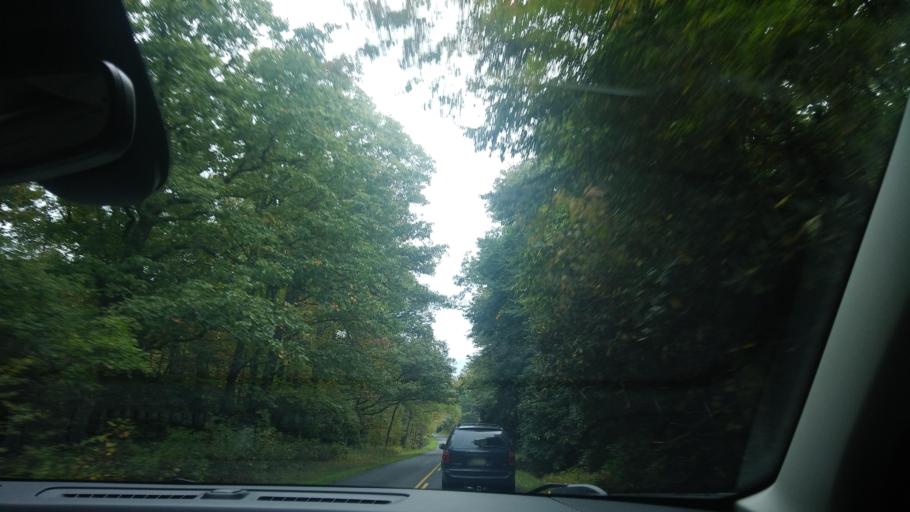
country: US
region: Virginia
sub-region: Carroll County
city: Cana
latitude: 36.6555
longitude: -80.5636
